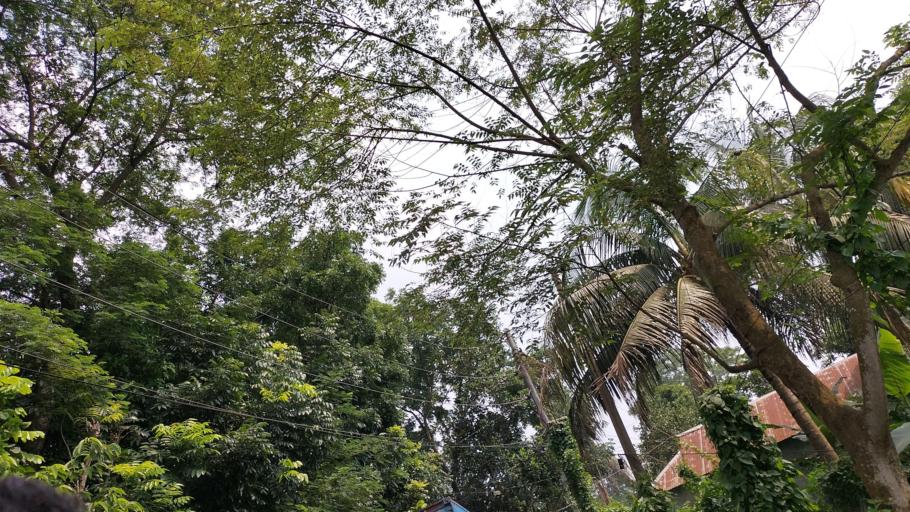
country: BD
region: Dhaka
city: Azimpur
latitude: 23.7186
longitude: 90.2771
